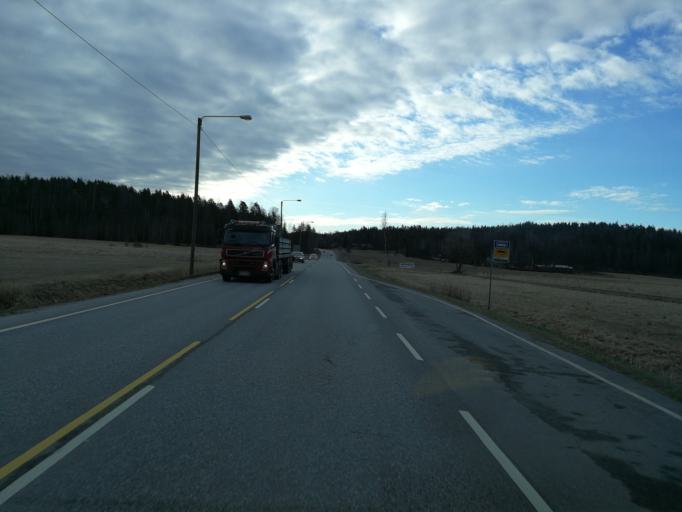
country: FI
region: Varsinais-Suomi
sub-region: Turku
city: Piikkioe
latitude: 60.4338
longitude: 22.5931
